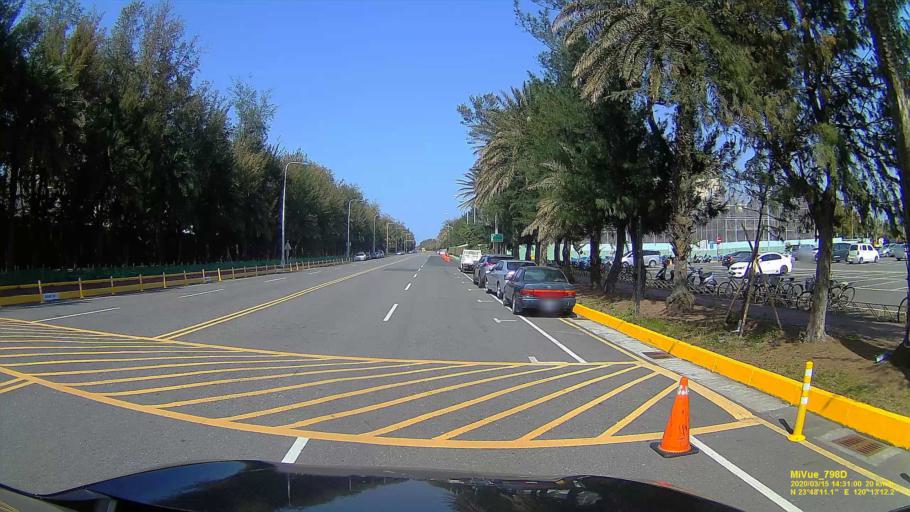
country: TW
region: Taiwan
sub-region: Yunlin
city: Douliu
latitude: 23.8032
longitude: 120.2201
